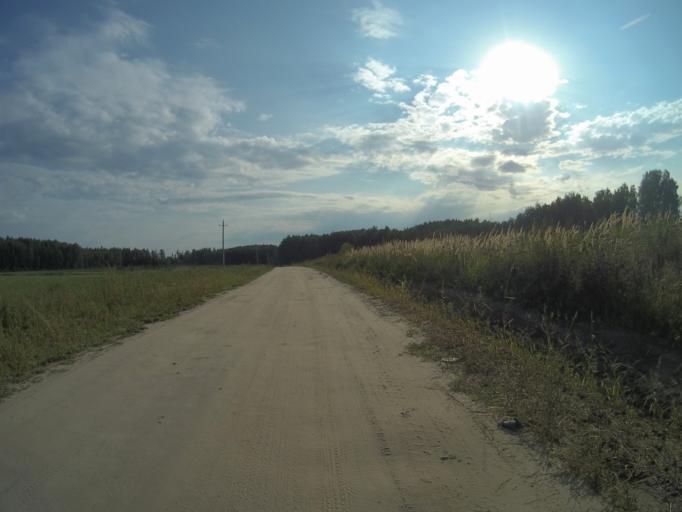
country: RU
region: Vladimir
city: Raduzhnyy
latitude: 55.9887
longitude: 40.2151
